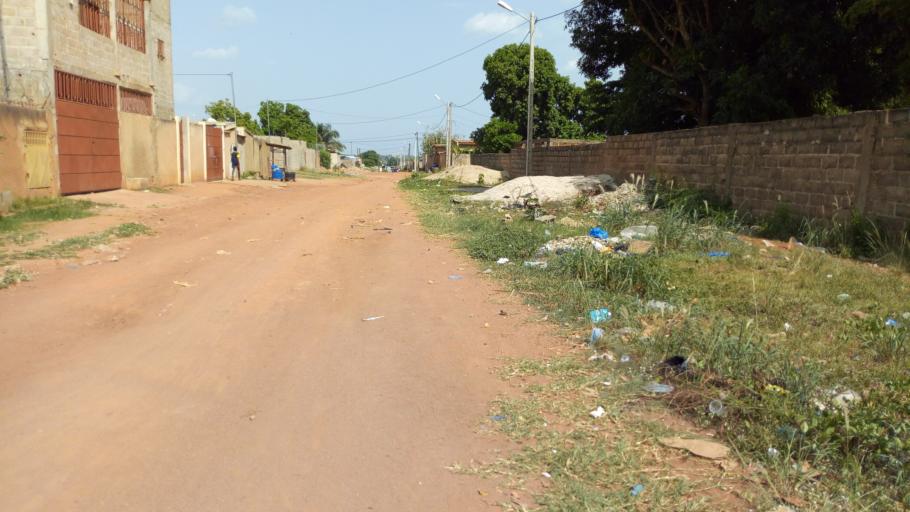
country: CI
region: Vallee du Bandama
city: Bouake
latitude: 7.7109
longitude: -5.0438
